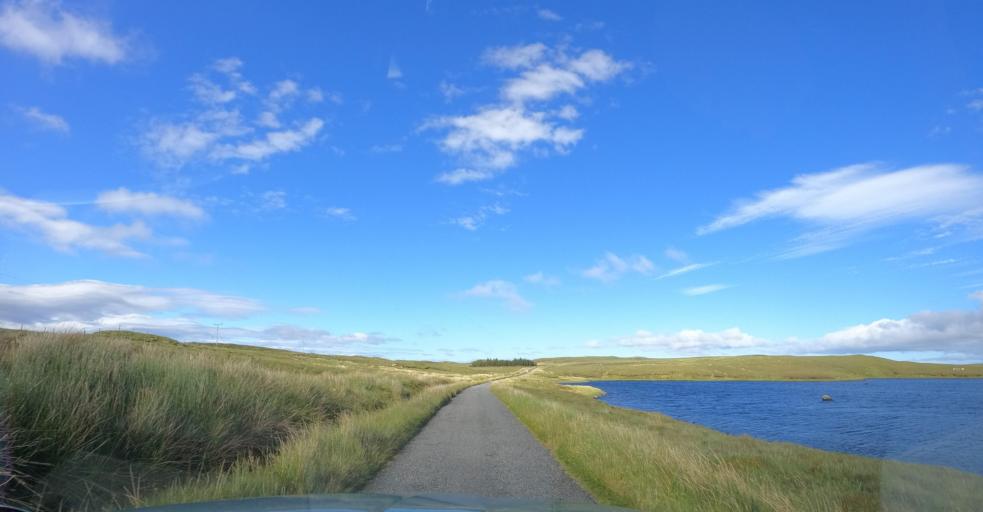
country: GB
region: Scotland
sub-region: Eilean Siar
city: Stornoway
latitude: 58.1782
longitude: -6.5506
